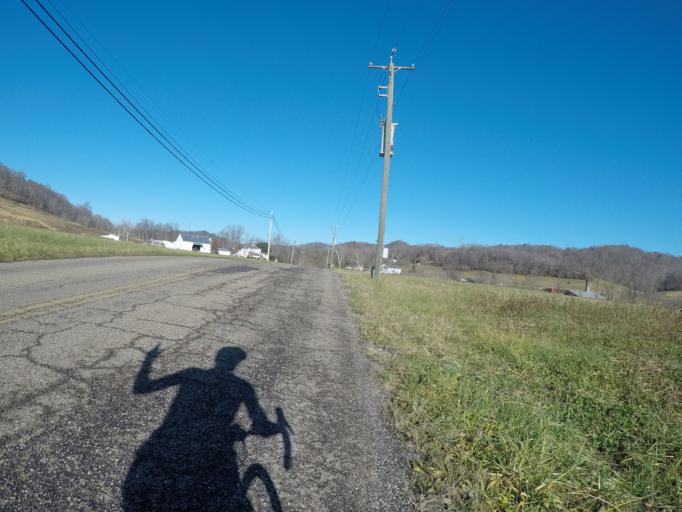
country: US
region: West Virginia
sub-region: Cabell County
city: Huntington
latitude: 38.4836
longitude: -82.4683
